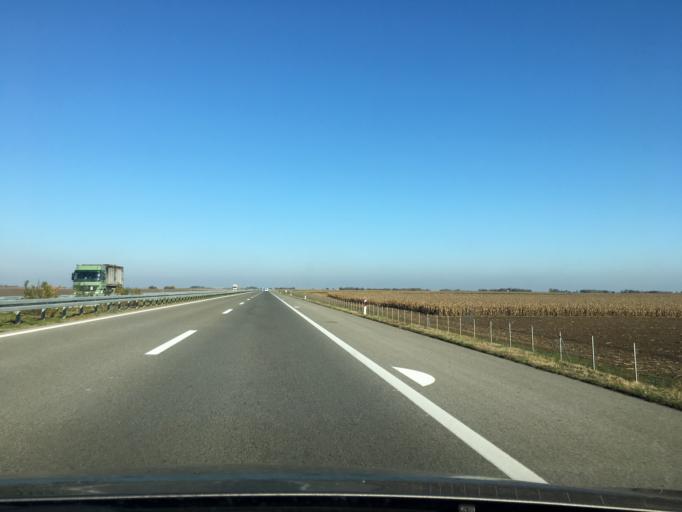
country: RS
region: Autonomna Pokrajina Vojvodina
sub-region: Severnobacki Okrug
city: Mali Igos
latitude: 45.7614
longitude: 19.7015
